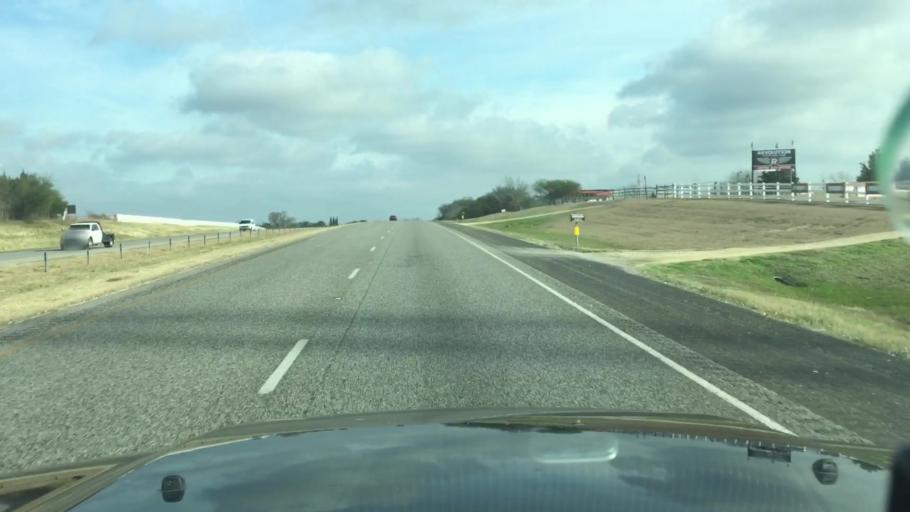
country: US
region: Texas
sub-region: Washington County
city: Brenham
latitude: 30.1348
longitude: -96.2495
